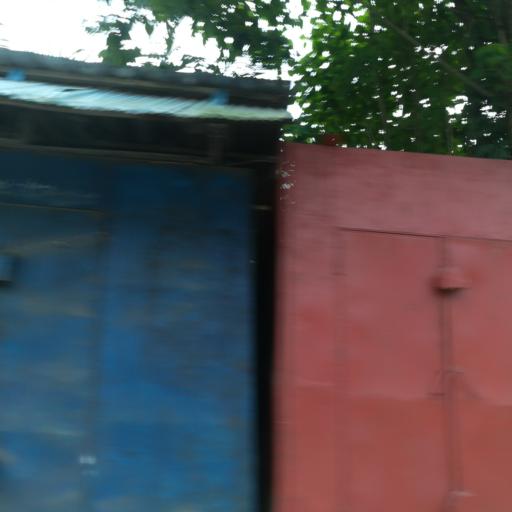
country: NG
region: Rivers
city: Port Harcourt
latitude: 4.8104
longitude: 7.0474
